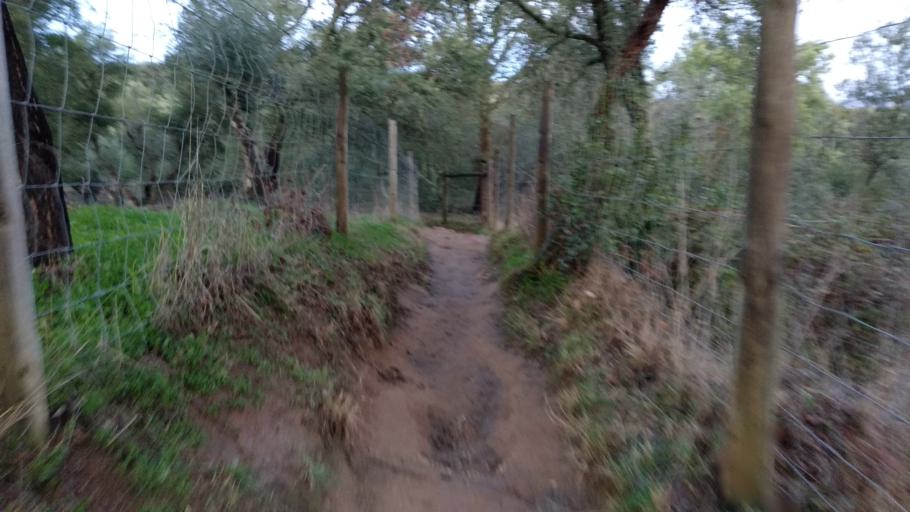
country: PT
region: Evora
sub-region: Evora
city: Evora
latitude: 38.5644
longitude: -8.0477
